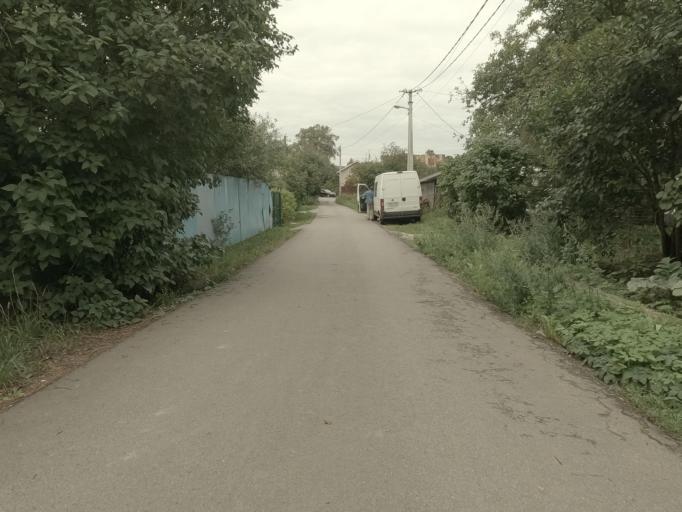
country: RU
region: Leningrad
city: Koltushi
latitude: 59.8974
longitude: 30.6713
